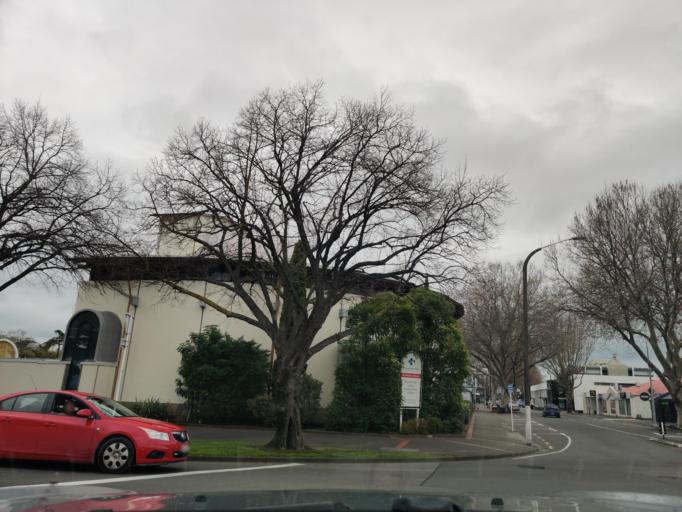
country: NZ
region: Hawke's Bay
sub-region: Napier City
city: Napier
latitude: -39.4932
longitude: 176.9140
